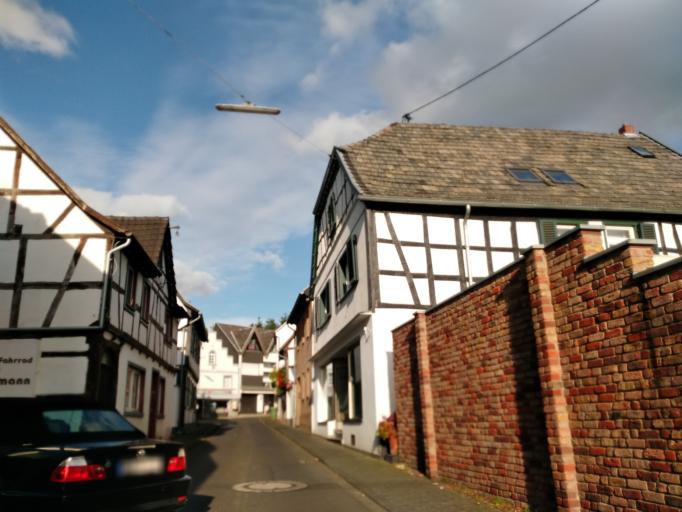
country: DE
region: Rheinland-Pfalz
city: Rheinbreitbach
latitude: 50.6191
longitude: 7.2307
